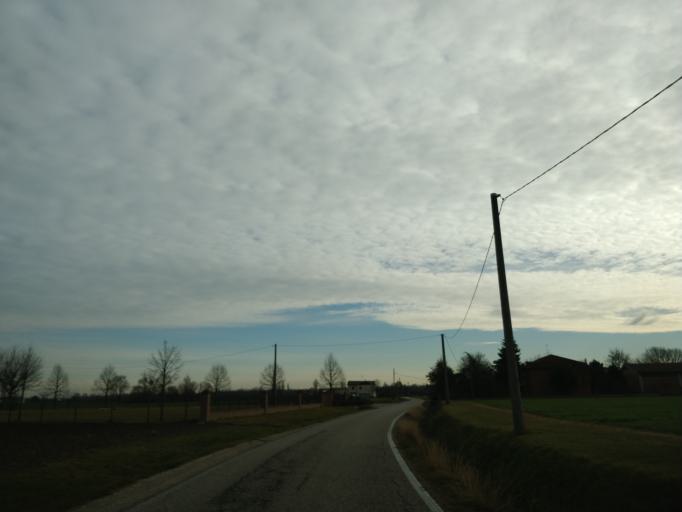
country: IT
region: Emilia-Romagna
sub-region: Provincia di Bologna
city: Argelato
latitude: 44.6128
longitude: 11.3377
